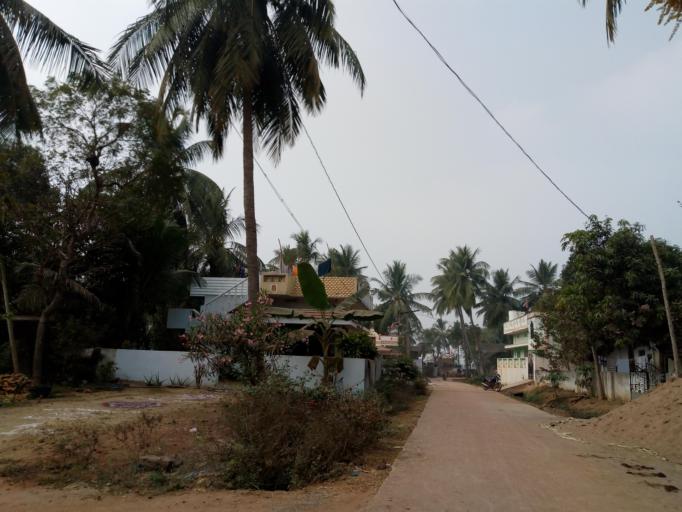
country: IN
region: Andhra Pradesh
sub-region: West Godavari
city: Tadepallegudem
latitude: 16.8622
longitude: 81.3160
